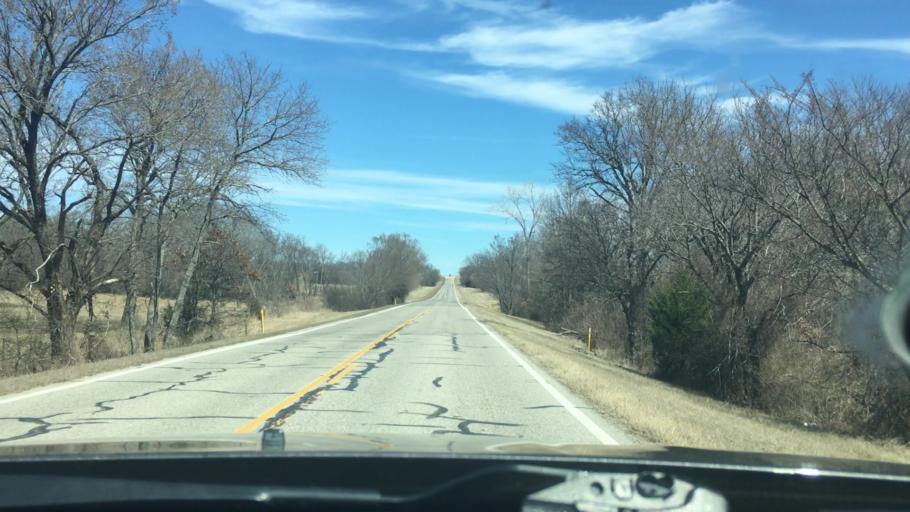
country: US
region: Oklahoma
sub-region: Carter County
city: Dickson
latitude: 34.3245
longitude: -96.9581
